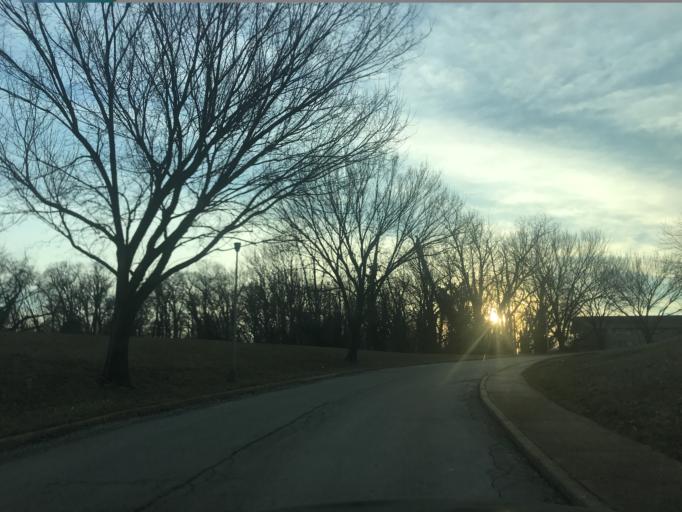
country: US
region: Maryland
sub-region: Baltimore County
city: Charlestown
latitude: 39.2636
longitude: -76.7182
